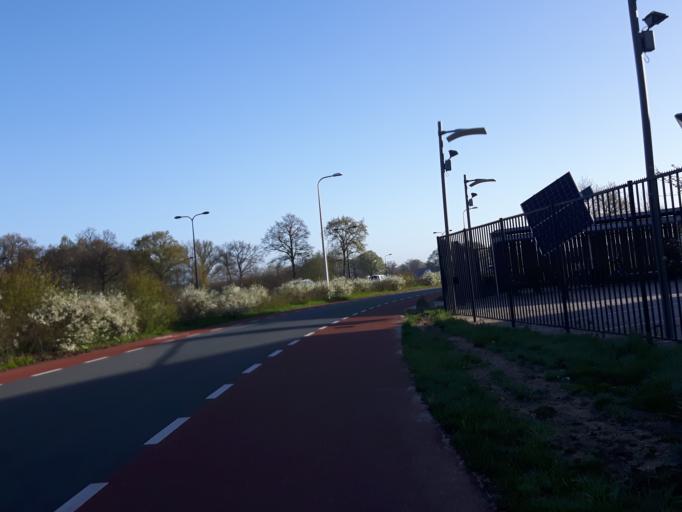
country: NL
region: Overijssel
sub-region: Gemeente Hengelo
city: Hengelo
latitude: 52.2218
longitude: 6.8342
